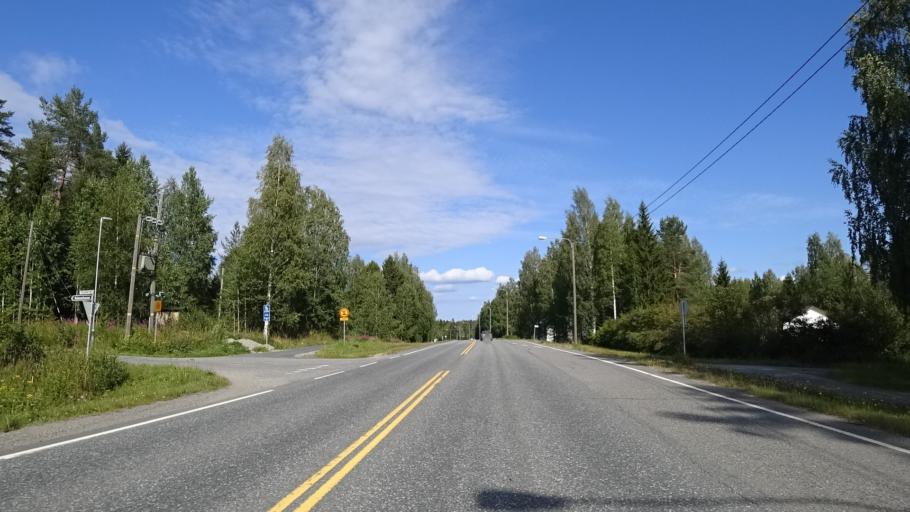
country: FI
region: North Karelia
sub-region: Joensuu
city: Eno
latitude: 62.7986
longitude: 30.1071
